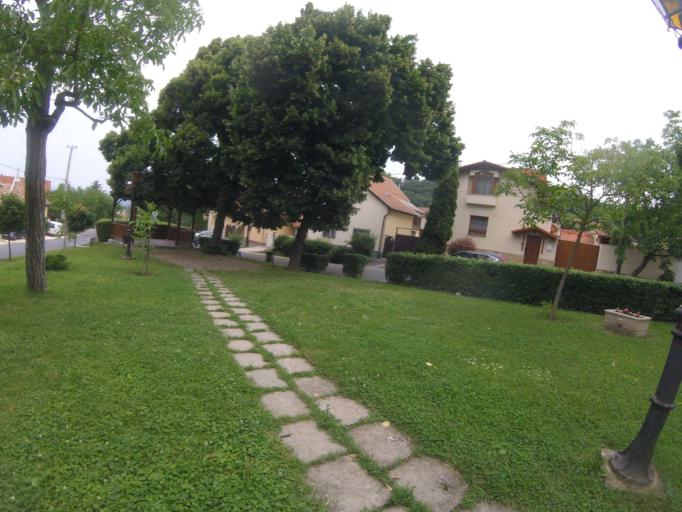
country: HU
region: Pest
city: Toeroekbalint
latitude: 47.4259
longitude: 18.9120
